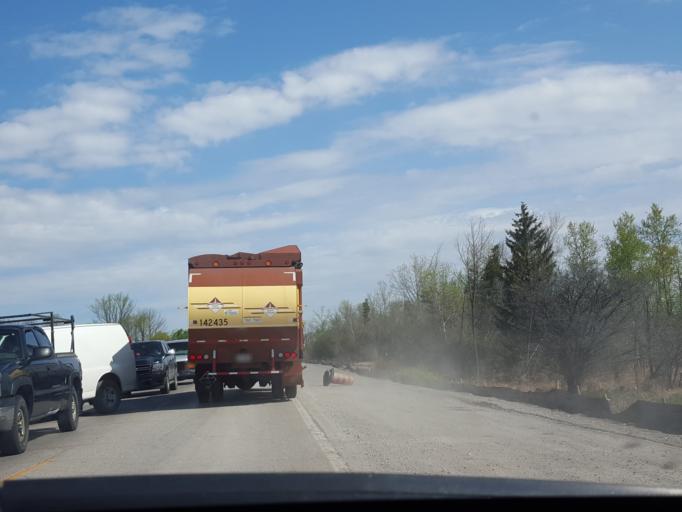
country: CA
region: Ontario
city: Uxbridge
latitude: 44.0783
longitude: -78.9370
